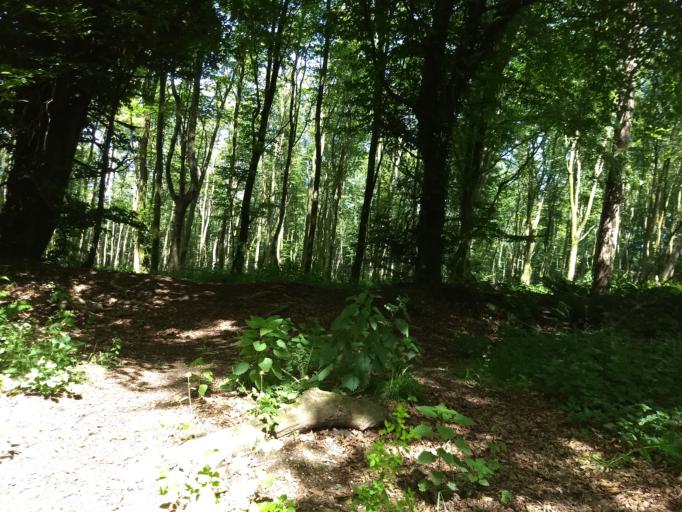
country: GB
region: England
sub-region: Isle of Wight
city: Shalfleet
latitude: 50.6642
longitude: -1.3813
